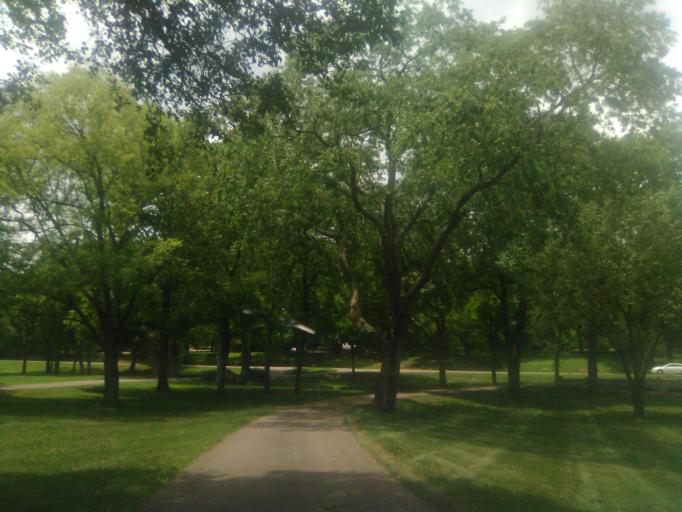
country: US
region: Tennessee
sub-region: Davidson County
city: Belle Meade
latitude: 36.0830
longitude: -86.8608
